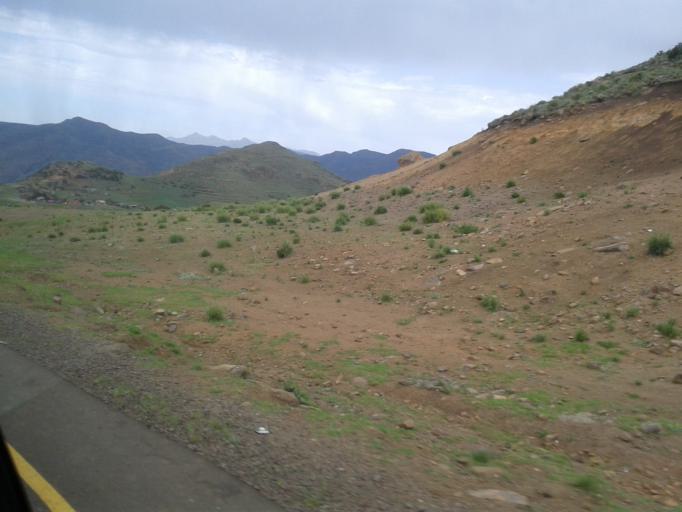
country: LS
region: Maseru
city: Nako
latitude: -29.6569
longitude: 27.8634
